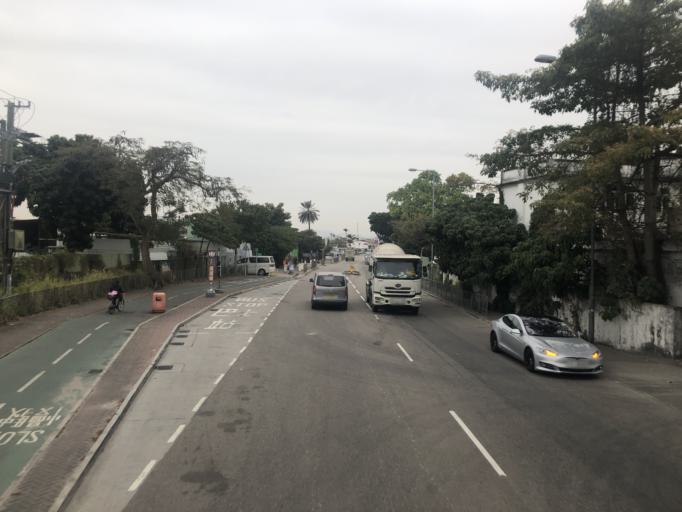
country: HK
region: Yuen Long
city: Yuen Long Kau Hui
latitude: 22.4327
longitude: 113.9927
